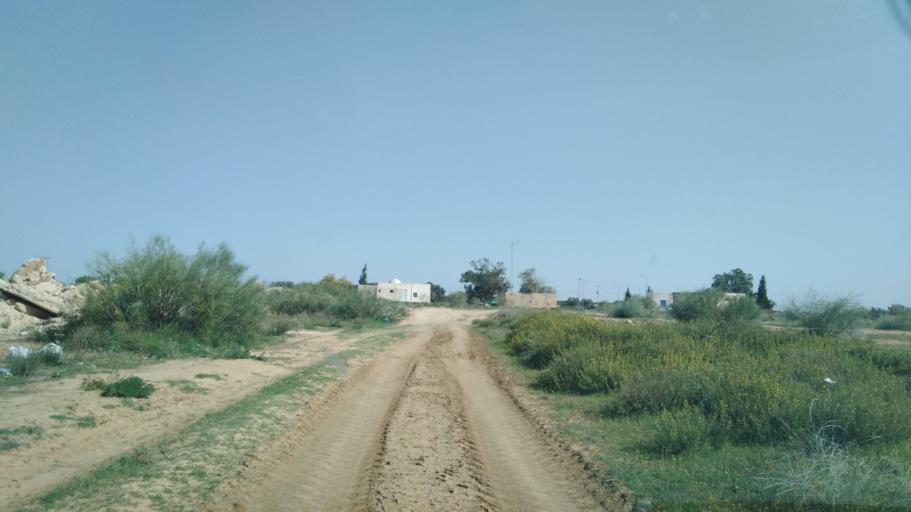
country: TN
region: Safaqis
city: Bi'r `Ali Bin Khalifah
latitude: 34.7789
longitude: 10.3652
